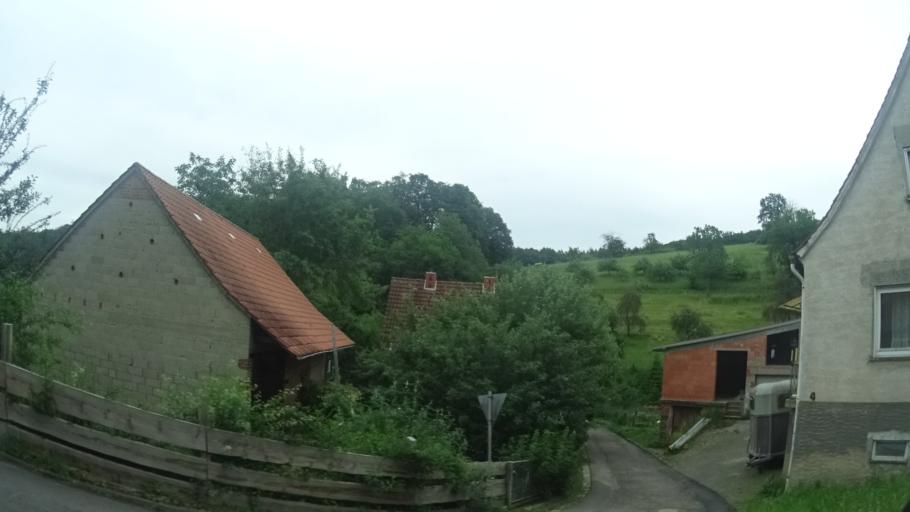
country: DE
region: Bavaria
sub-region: Regierungsbezirk Unterfranken
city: Johannesberg
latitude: 50.0702
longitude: 9.1148
